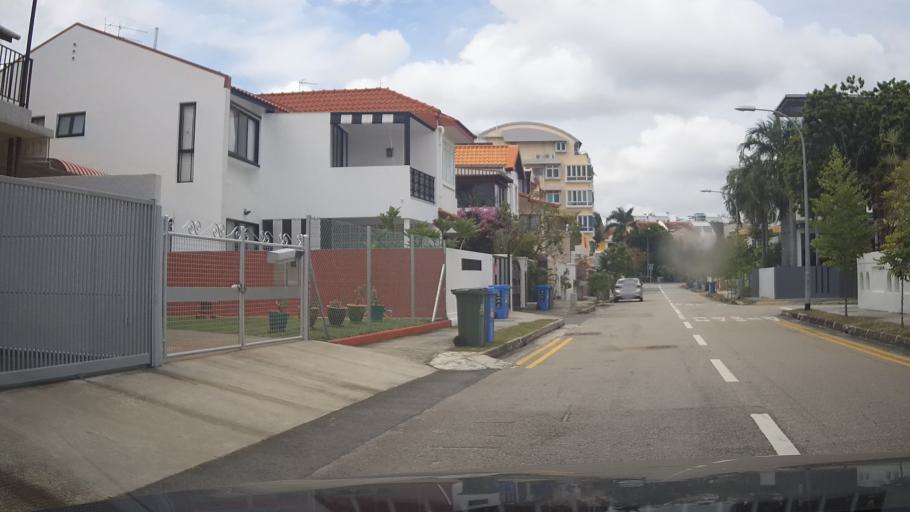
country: SG
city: Singapore
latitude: 1.3113
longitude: 103.9089
